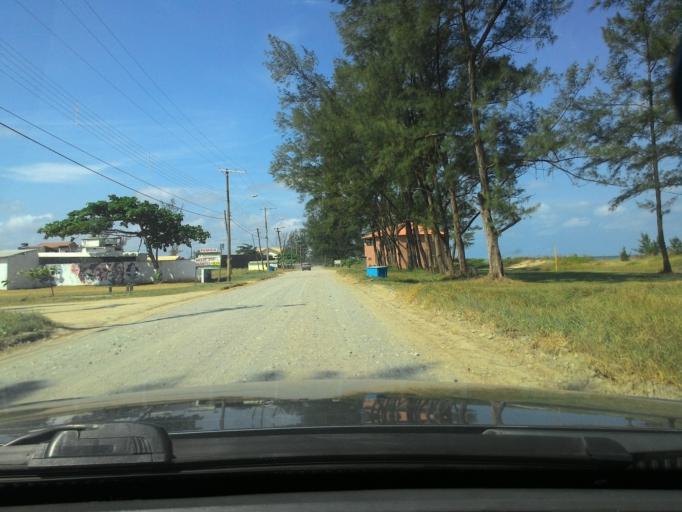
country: BR
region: Sao Paulo
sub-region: Iguape
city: Iguape
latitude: -24.8442
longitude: -47.6864
